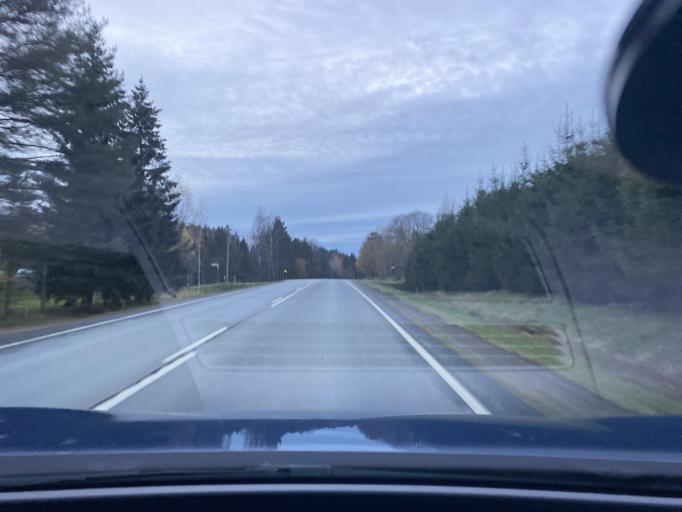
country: FI
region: Uusimaa
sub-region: Helsinki
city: Sammatti
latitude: 60.3846
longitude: 23.8887
